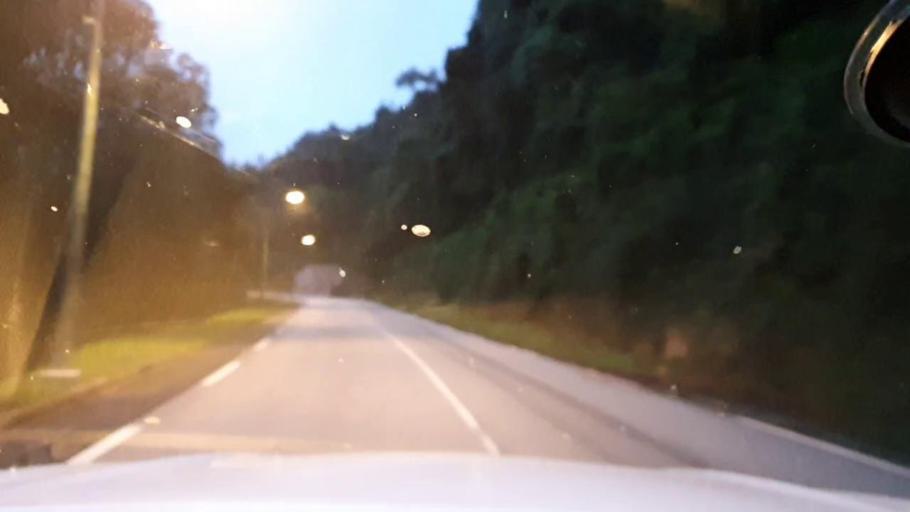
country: RW
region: Southern Province
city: Nzega
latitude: -2.5276
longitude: 29.3784
